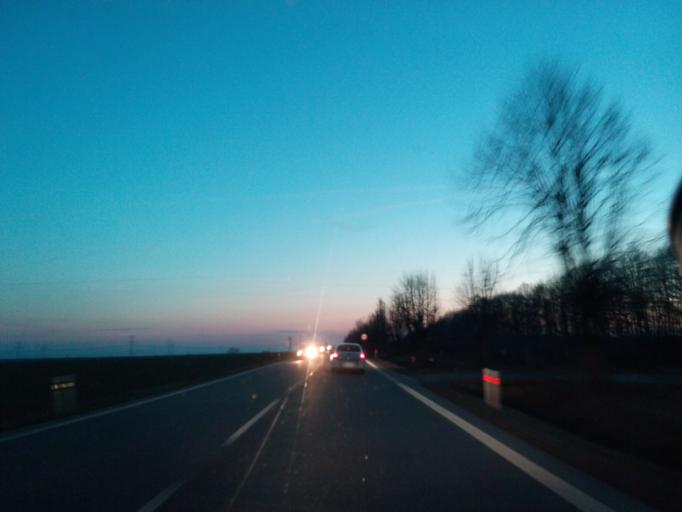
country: SK
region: Kosicky
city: Michalovce
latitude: 48.7176
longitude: 21.8435
